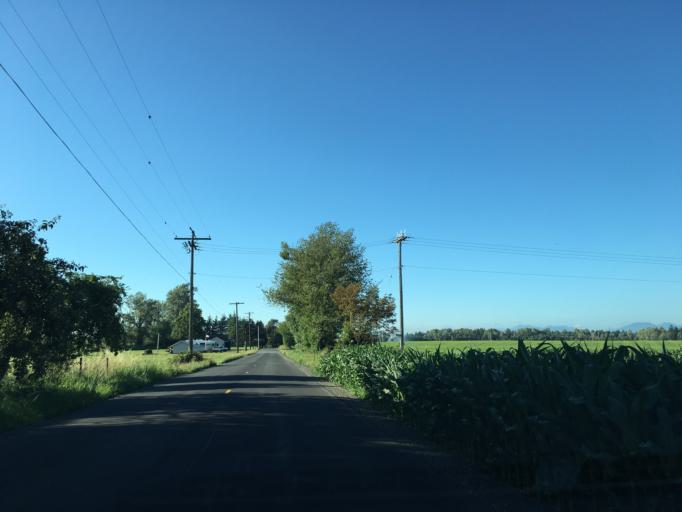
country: US
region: Washington
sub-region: Whatcom County
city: Everson
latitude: 48.9377
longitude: -122.3916
